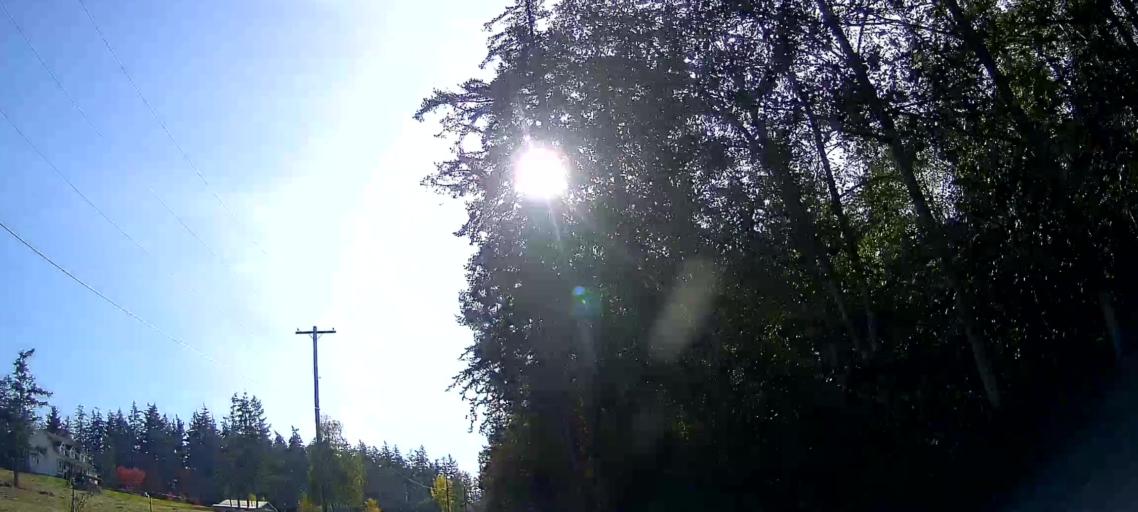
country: US
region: Washington
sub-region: Island County
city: Camano
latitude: 48.2022
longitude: -122.4564
